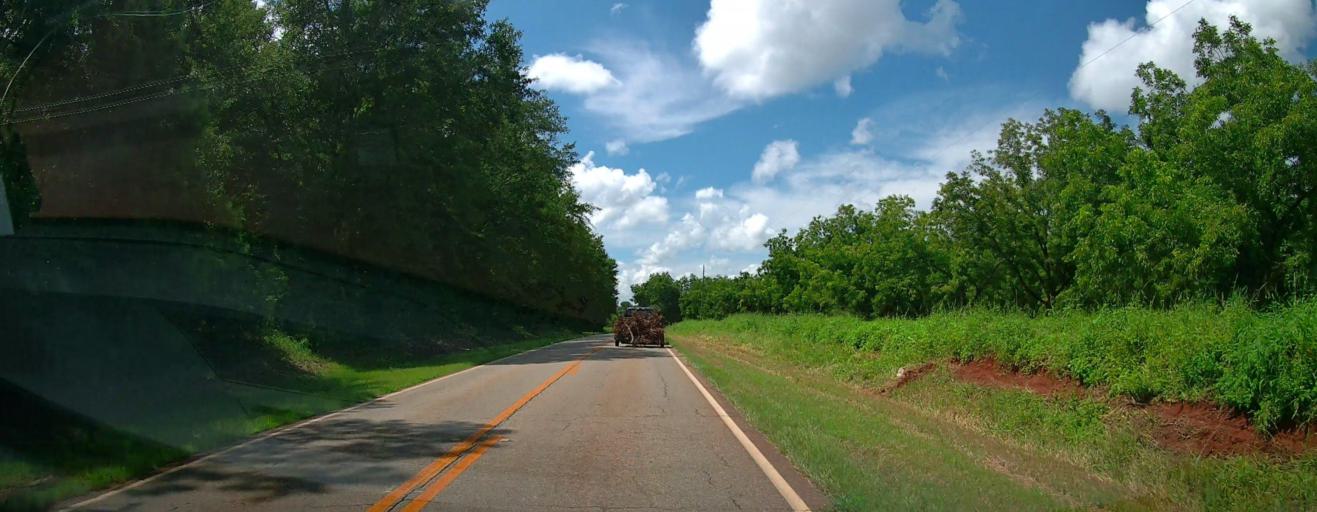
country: US
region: Georgia
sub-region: Houston County
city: Perry
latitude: 32.5212
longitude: -83.7743
